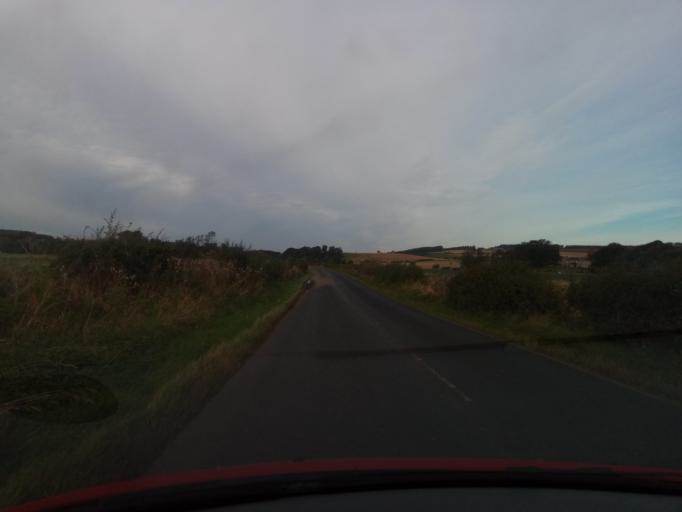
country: GB
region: Scotland
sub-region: The Scottish Borders
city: Kelso
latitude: 55.5209
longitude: -2.3964
